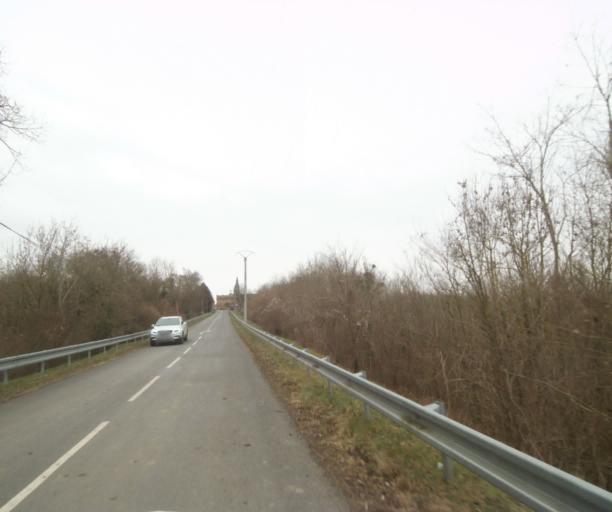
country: FR
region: Champagne-Ardenne
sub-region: Departement de la Haute-Marne
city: Villiers-en-Lieu
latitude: 48.6411
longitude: 4.7677
